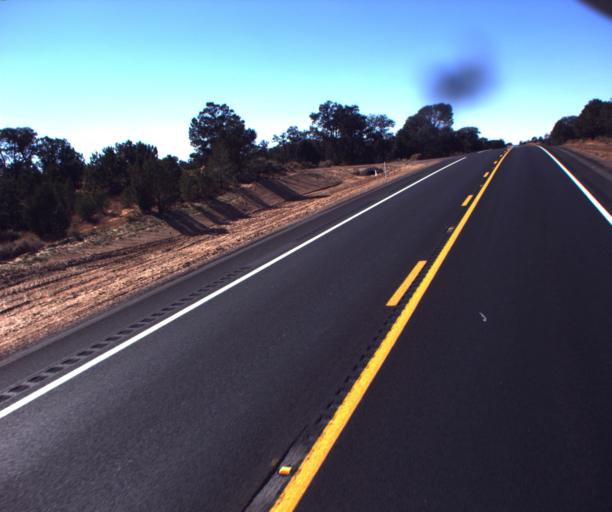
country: US
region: Arizona
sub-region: Apache County
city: Ganado
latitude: 35.7183
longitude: -109.3594
